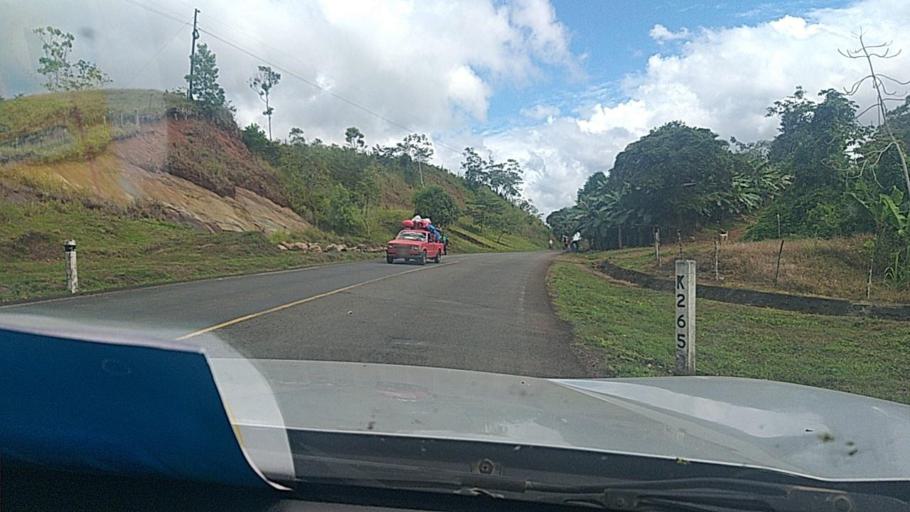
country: NI
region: Atlantico Sur
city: Muelle de los Bueyes
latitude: 12.1280
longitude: -84.4379
